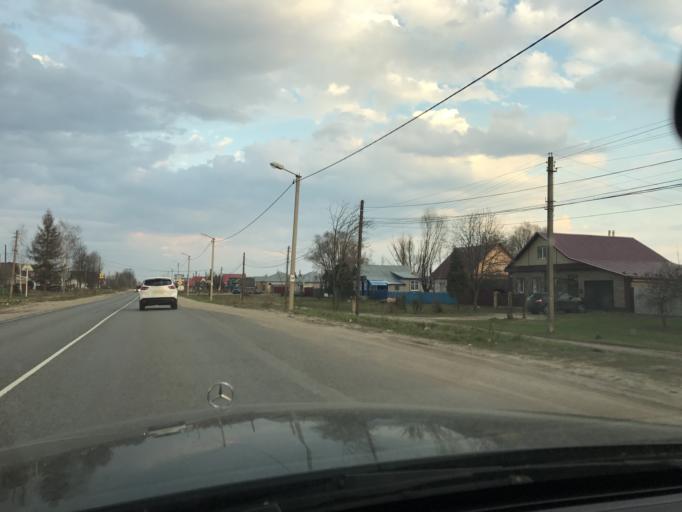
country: RU
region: Vladimir
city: Murom
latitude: 55.6096
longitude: 41.9529
